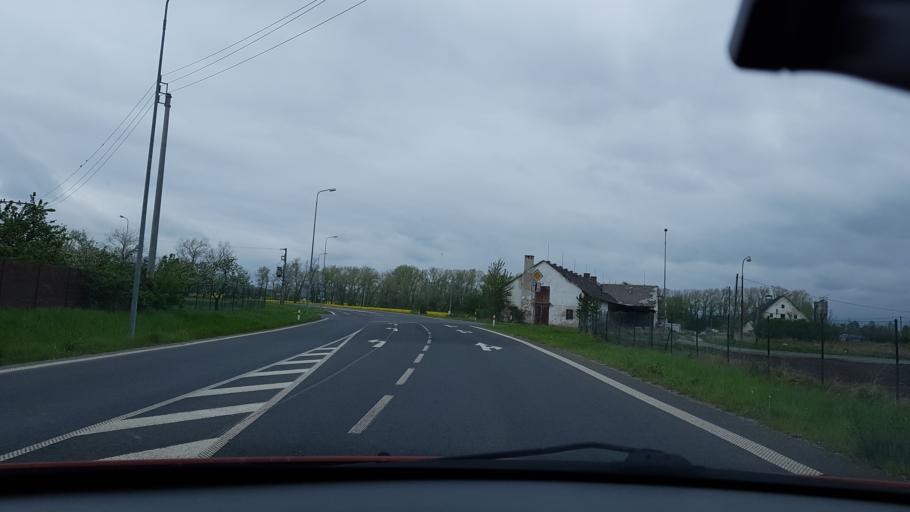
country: CZ
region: Olomoucky
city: Javornik
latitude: 50.3961
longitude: 17.0119
